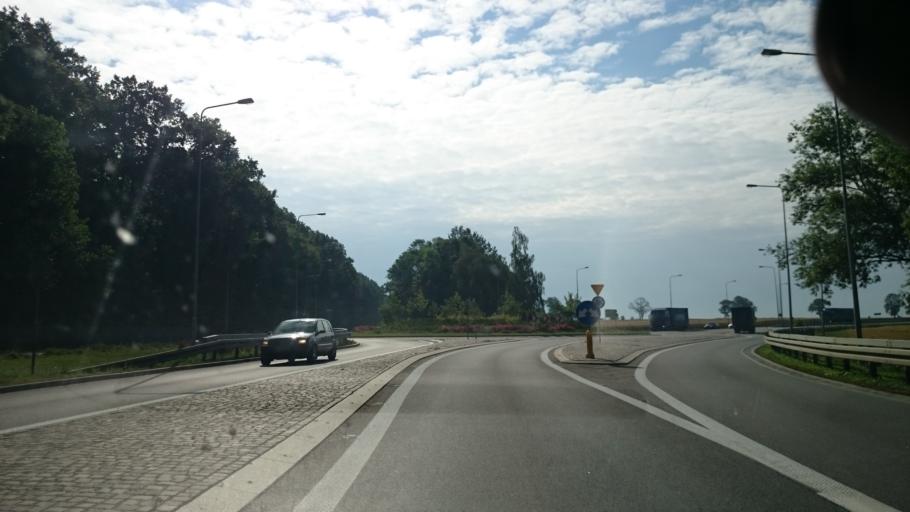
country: PL
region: Opole Voivodeship
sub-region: Powiat strzelecki
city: Strzelce Opolskie
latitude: 50.5025
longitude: 18.3353
